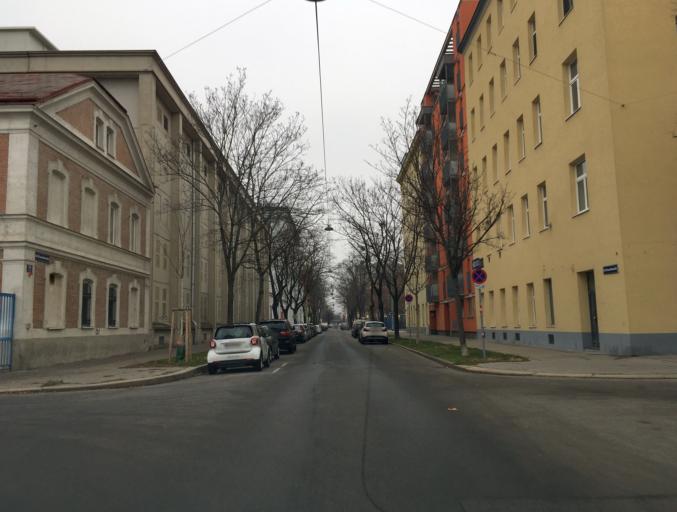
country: AT
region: Vienna
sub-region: Wien Stadt
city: Vienna
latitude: 48.2328
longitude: 16.3871
